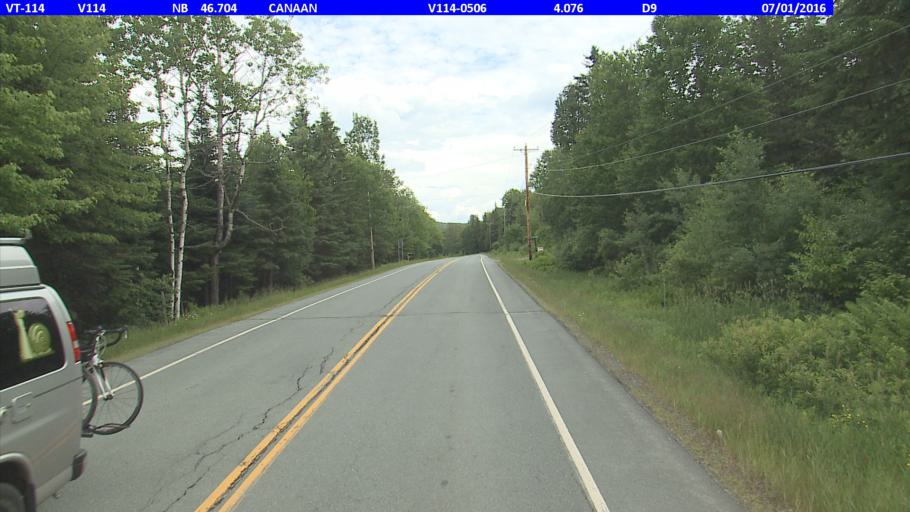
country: US
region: New Hampshire
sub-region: Coos County
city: Colebrook
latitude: 45.0090
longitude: -71.6125
